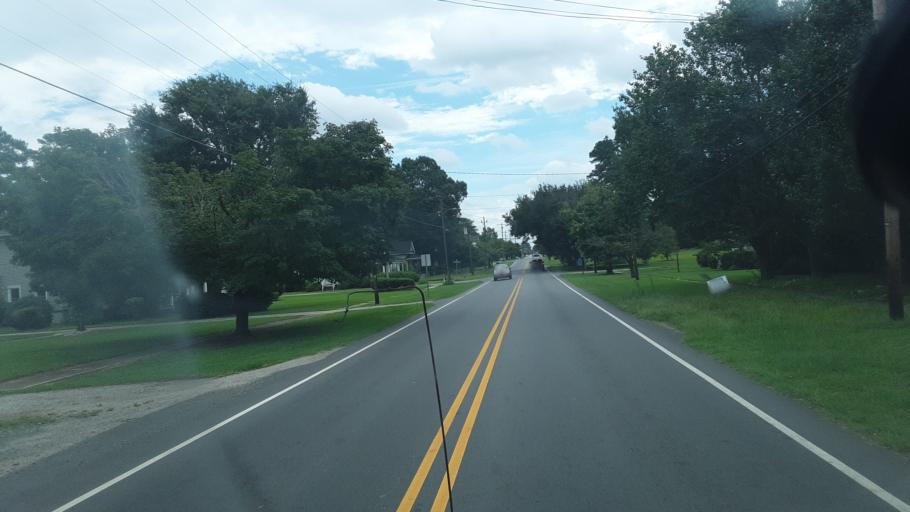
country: US
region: North Carolina
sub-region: Robeson County
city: Rowland
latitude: 34.5406
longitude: -79.3003
